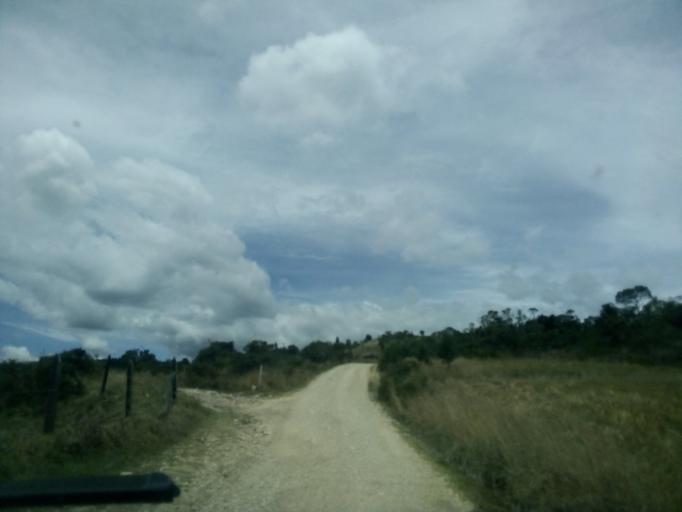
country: CO
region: Boyaca
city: Toca
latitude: 5.6229
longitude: -73.1279
